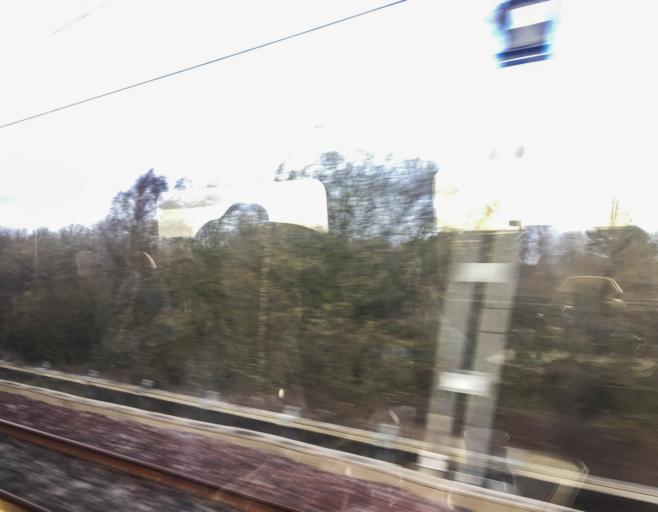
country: GB
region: Scotland
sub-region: Dumfries and Galloway
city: Gretna
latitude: 54.9869
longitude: -3.0316
